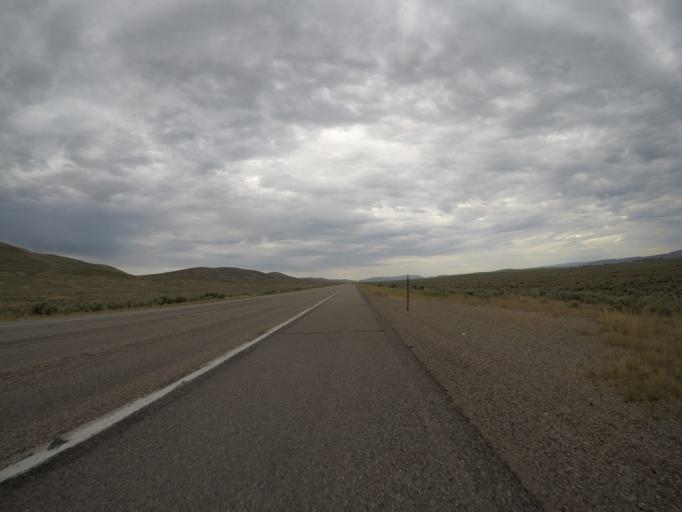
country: US
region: Utah
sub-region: Rich County
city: Randolph
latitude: 41.8856
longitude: -110.9631
